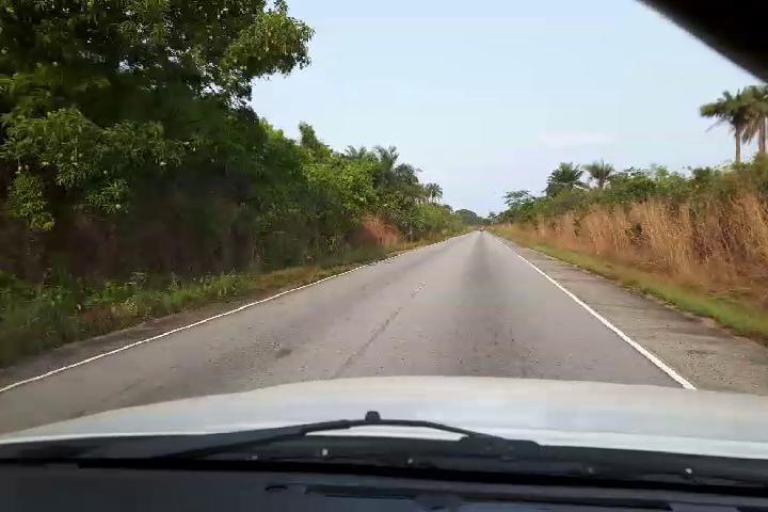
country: SL
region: Southern Province
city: Baoma
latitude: 7.9245
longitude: -11.5374
